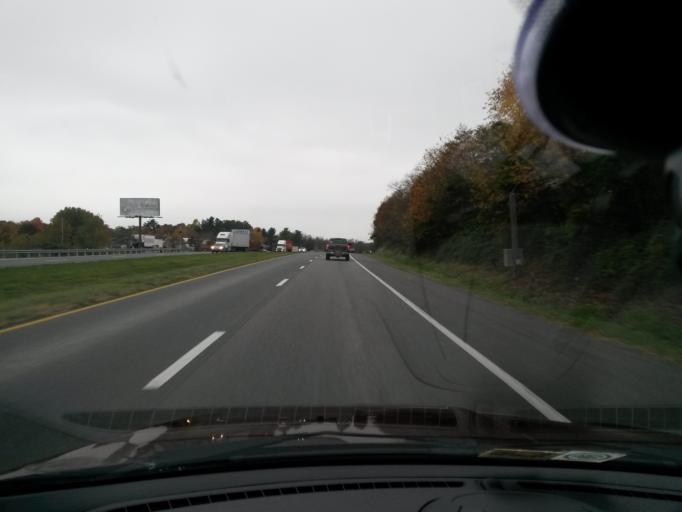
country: US
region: Virginia
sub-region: Roanoke County
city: Vinton
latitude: 37.3201
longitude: -79.8746
